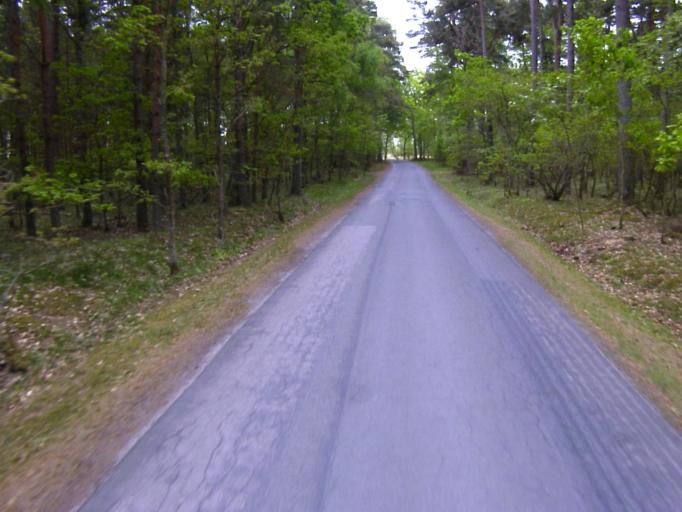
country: SE
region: Skane
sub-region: Kristianstads Kommun
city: Ahus
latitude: 55.9214
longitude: 14.3176
